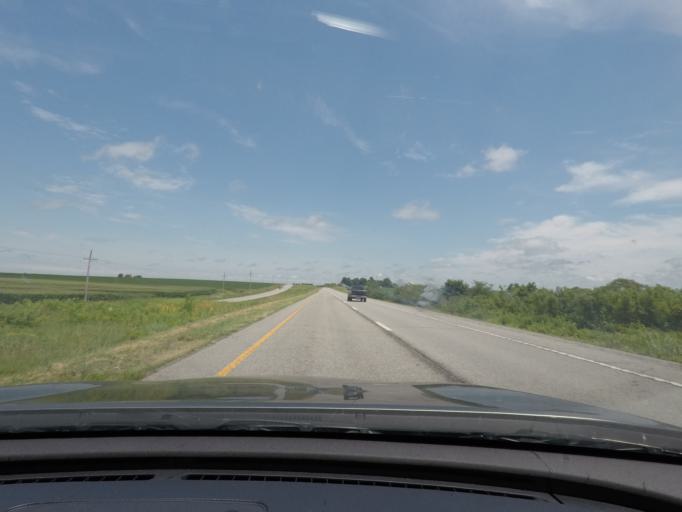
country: US
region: Missouri
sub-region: Saline County
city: Marshall
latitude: 39.0482
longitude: -93.1945
